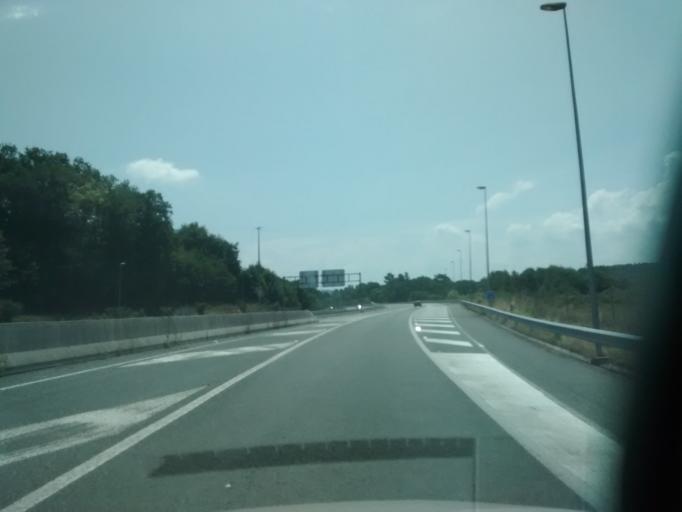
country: ES
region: Galicia
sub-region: Provincia de Ourense
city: Maside
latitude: 42.4058
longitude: -8.0114
